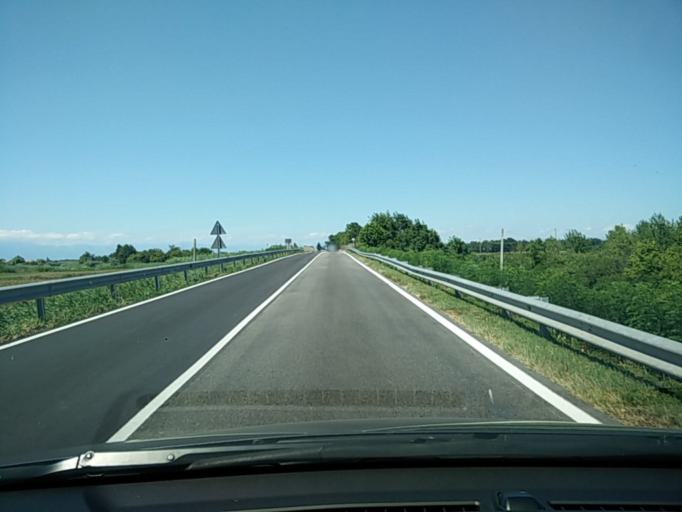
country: IT
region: Veneto
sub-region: Provincia di Venezia
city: La Salute di Livenza
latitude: 45.6884
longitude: 12.8447
